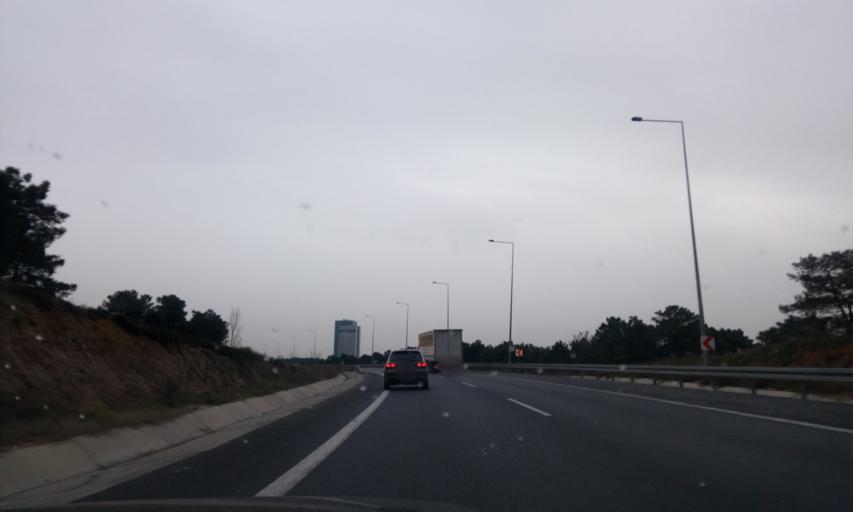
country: TR
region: Istanbul
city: Umraniye
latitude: 41.0471
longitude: 29.1203
